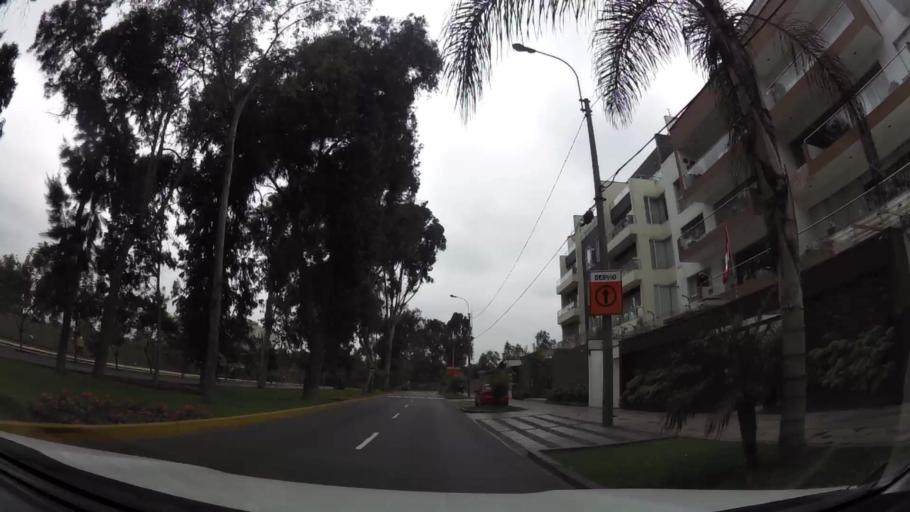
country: PE
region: Lima
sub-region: Lima
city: San Luis
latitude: -12.1045
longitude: -76.9849
